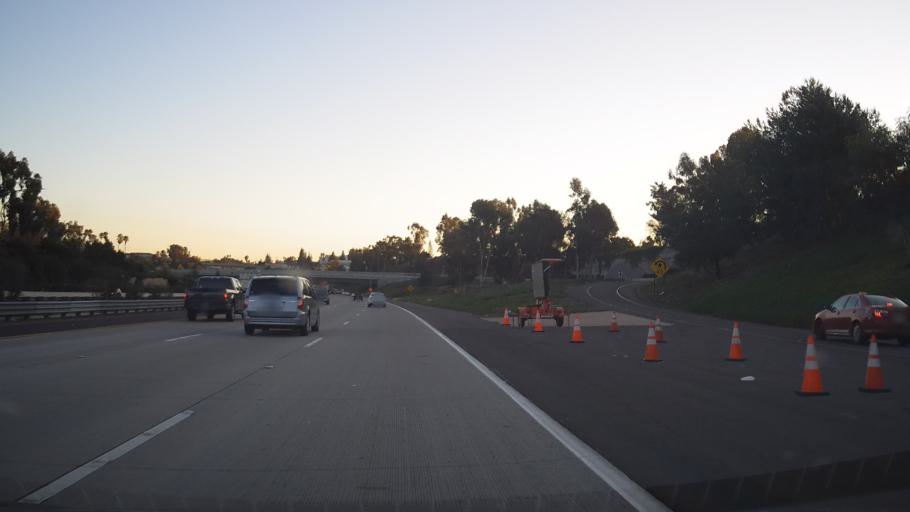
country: US
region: California
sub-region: San Diego County
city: La Mesa
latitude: 32.7904
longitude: -117.0067
